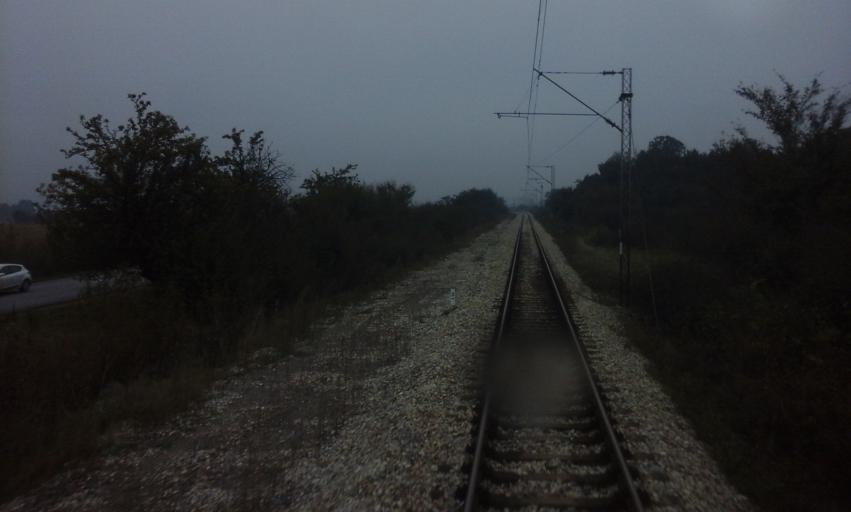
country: RS
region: Central Serbia
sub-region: Pomoravski Okrug
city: Paracin
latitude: 43.8899
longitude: 21.3824
